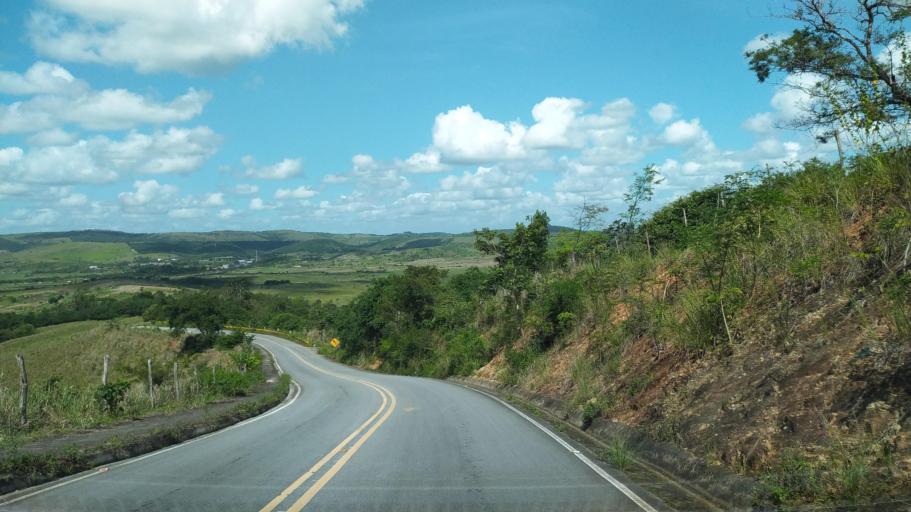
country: BR
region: Alagoas
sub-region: Uniao Dos Palmares
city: Uniao dos Palmares
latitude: -9.1666
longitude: -36.0655
